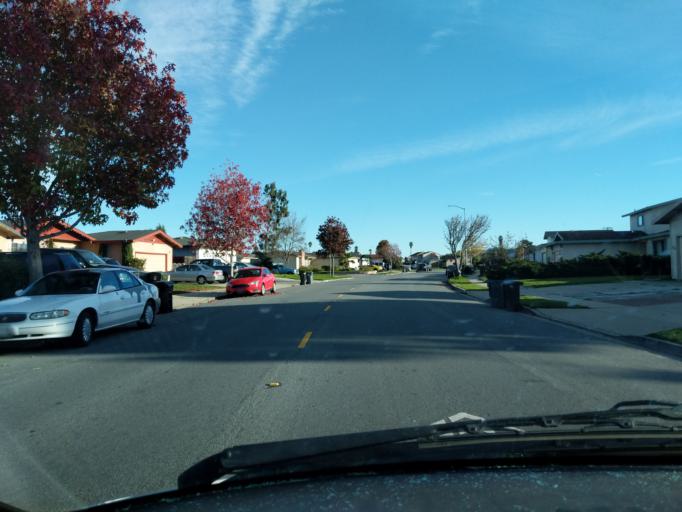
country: US
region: California
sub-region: Monterey County
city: Boronda
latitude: 36.7065
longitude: -121.6617
